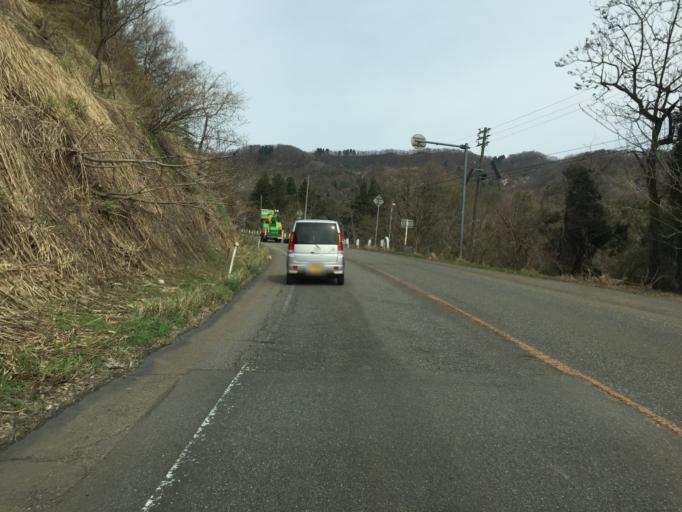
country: JP
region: Niigata
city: Nagaoka
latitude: 37.4550
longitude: 138.9162
